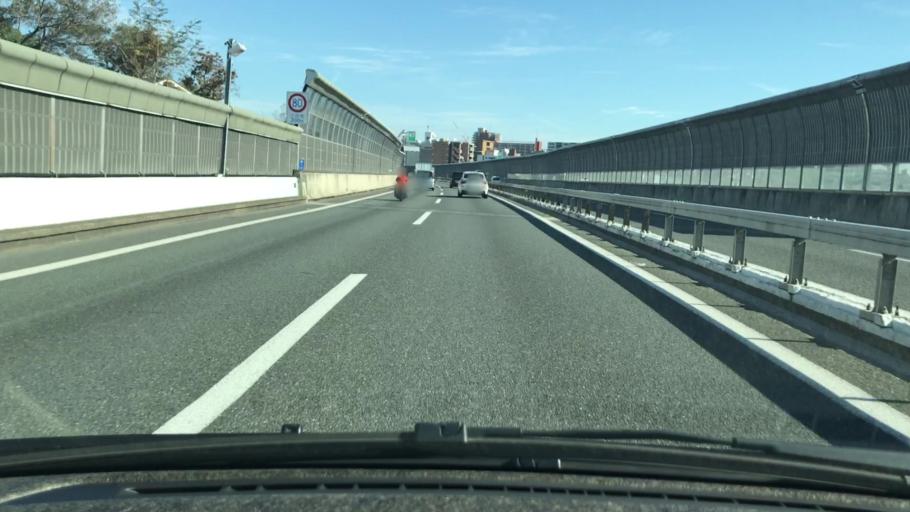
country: JP
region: Osaka
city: Suita
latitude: 34.7602
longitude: 135.4881
